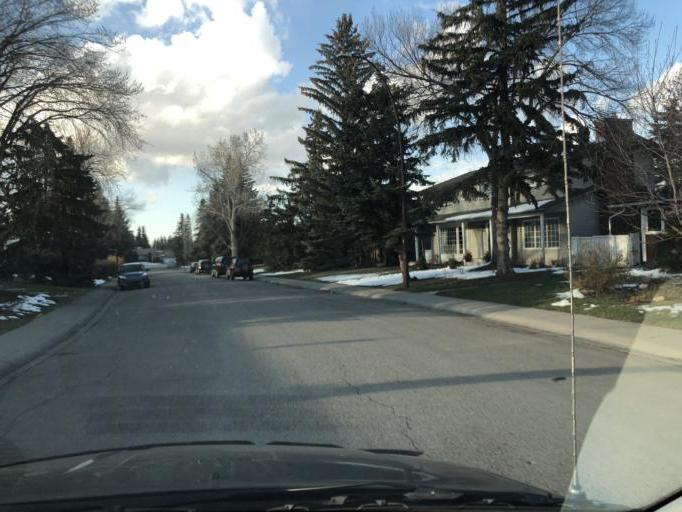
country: CA
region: Alberta
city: Calgary
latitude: 50.9401
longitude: -114.0363
